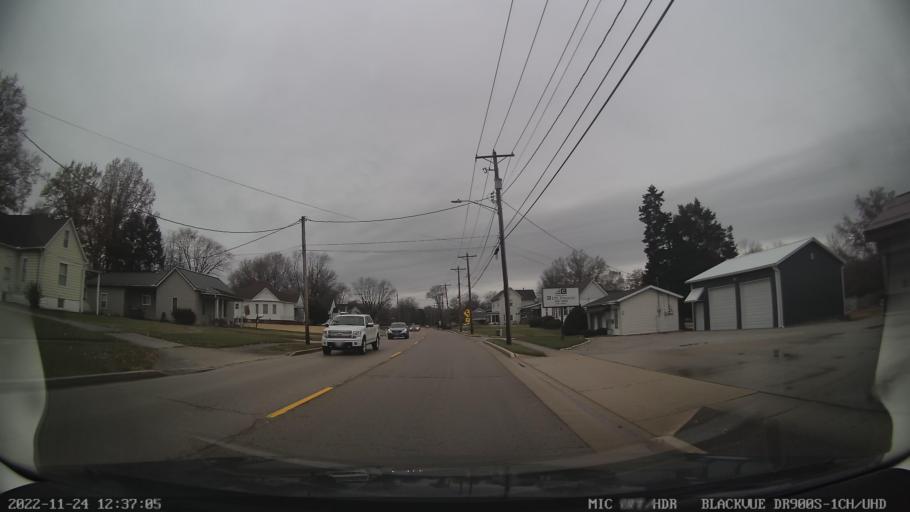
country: US
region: Illinois
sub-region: Macoupin County
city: Staunton
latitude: 39.0112
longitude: -89.7934
